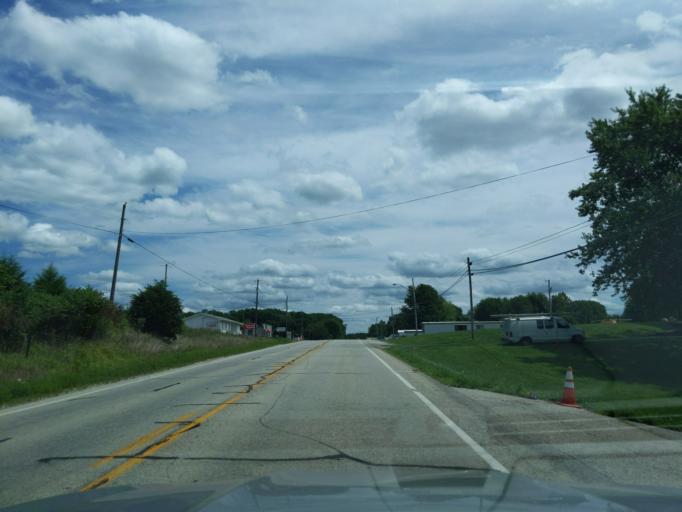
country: US
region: Indiana
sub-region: Ripley County
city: Batesville
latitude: 39.3085
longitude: -85.2501
